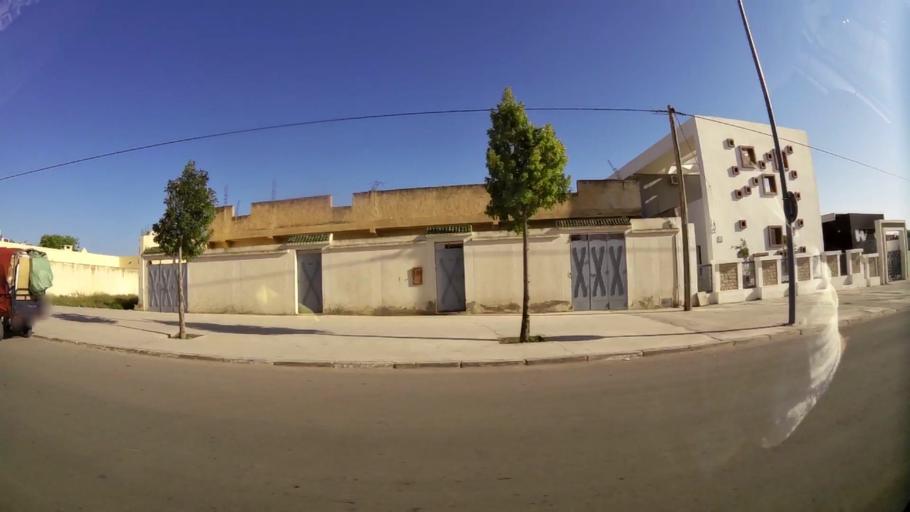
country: MA
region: Oriental
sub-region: Oujda-Angad
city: Oujda
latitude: 34.6973
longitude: -1.9173
